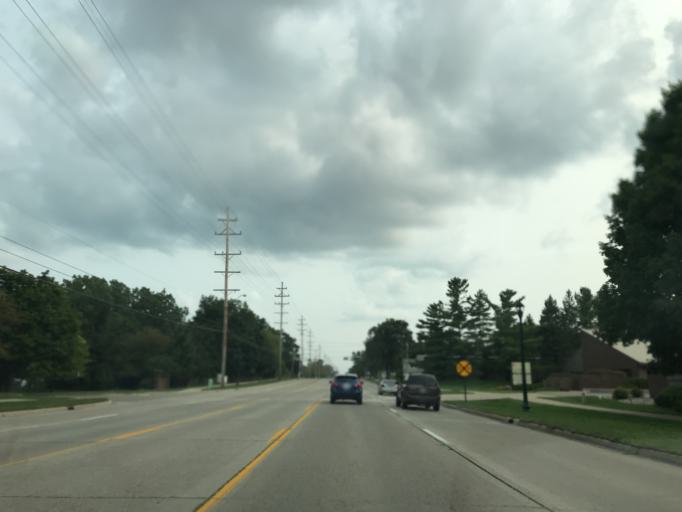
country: US
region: Michigan
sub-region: Ingham County
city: Okemos
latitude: 42.7061
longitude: -84.4325
